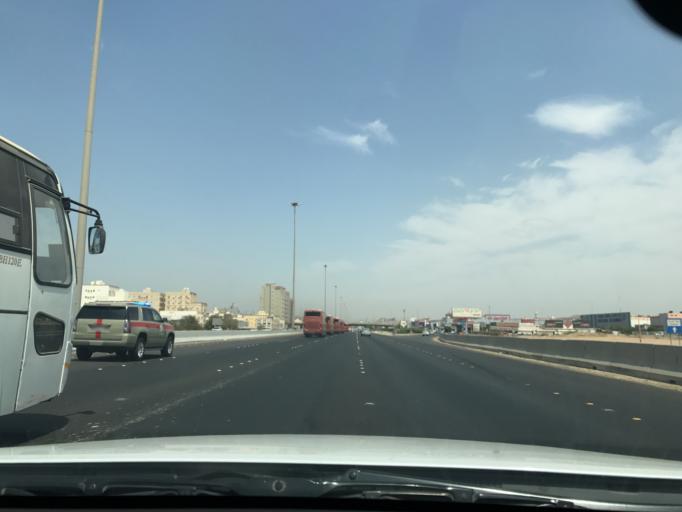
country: SA
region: Makkah
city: Jeddah
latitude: 21.4431
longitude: 39.2758
